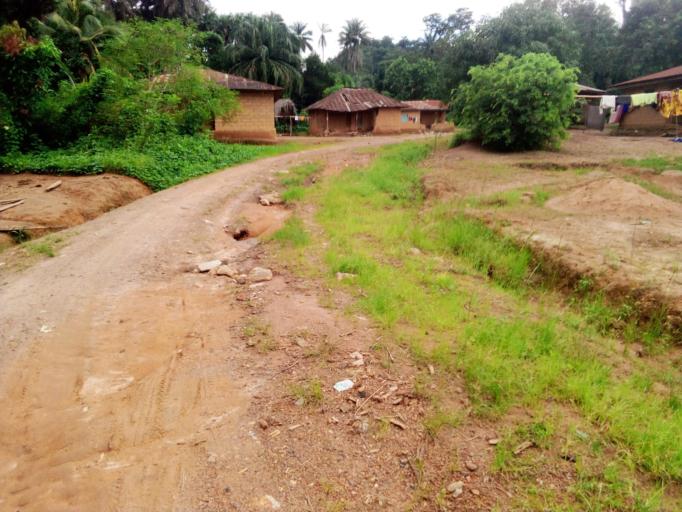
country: SL
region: Eastern Province
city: Giehun
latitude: 8.5628
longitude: -10.9961
